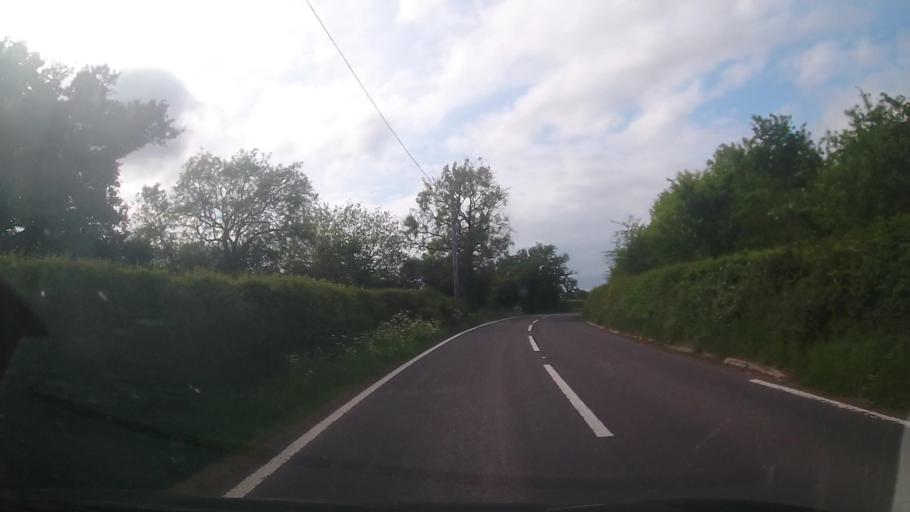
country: GB
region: England
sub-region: Shropshire
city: Petton
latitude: 52.8229
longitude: -2.8002
